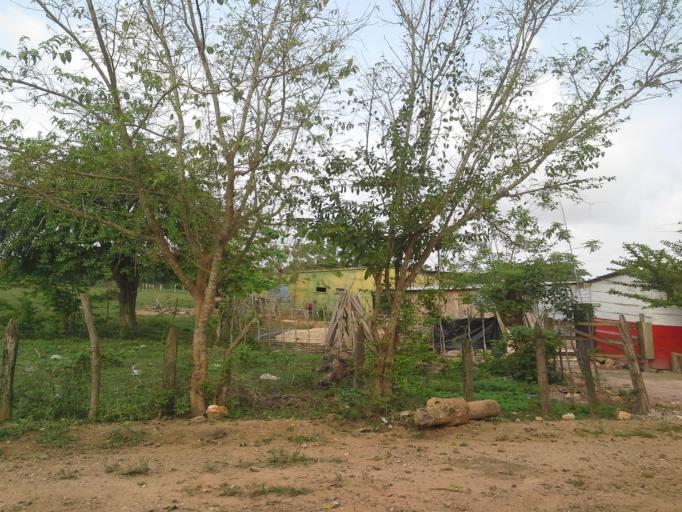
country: CO
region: Cordoba
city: Chima
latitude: 9.1497
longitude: -75.6198
